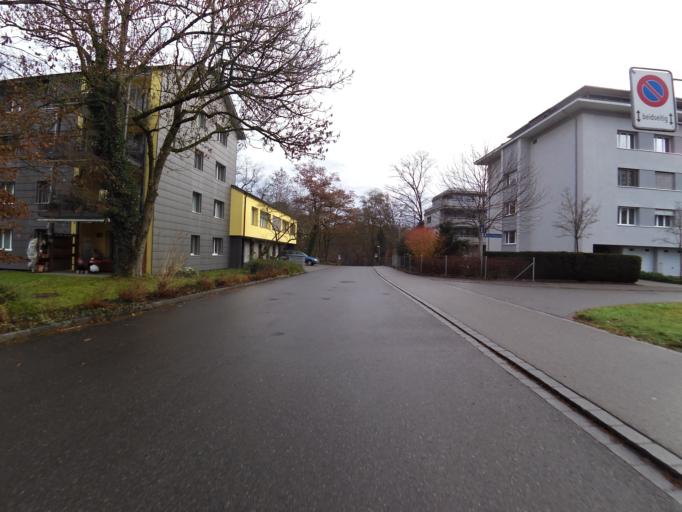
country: CH
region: Thurgau
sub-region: Frauenfeld District
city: Frauenfeld
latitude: 47.5510
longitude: 8.8937
